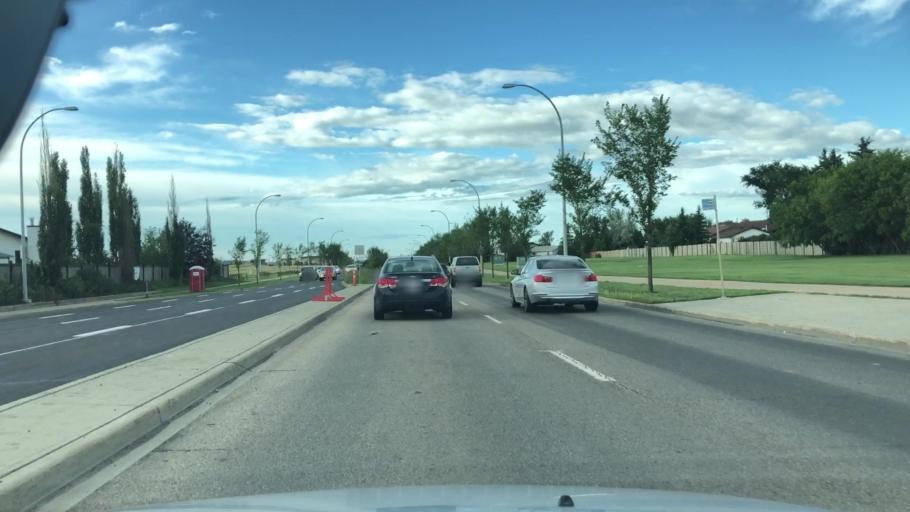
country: CA
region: Alberta
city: St. Albert
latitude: 53.6239
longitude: -113.5411
